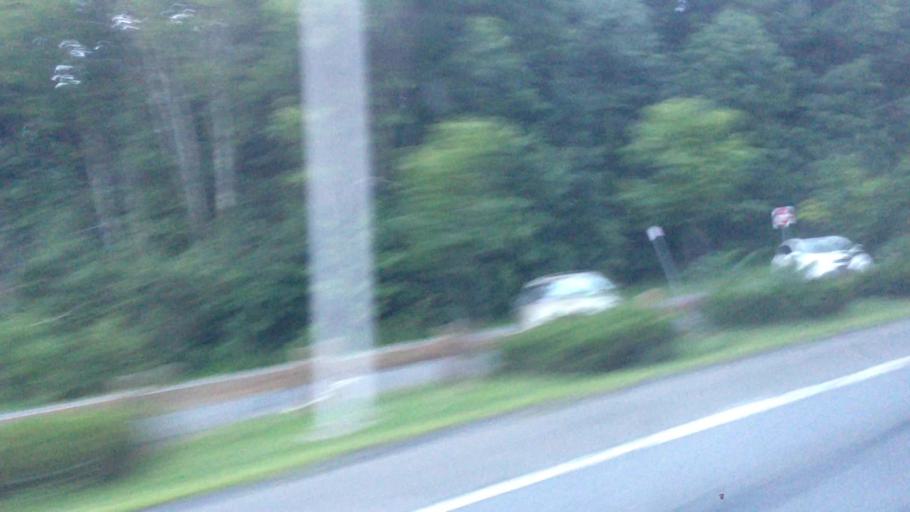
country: US
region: New York
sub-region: Dutchess County
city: Red Hook
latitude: 41.9729
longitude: -73.9159
